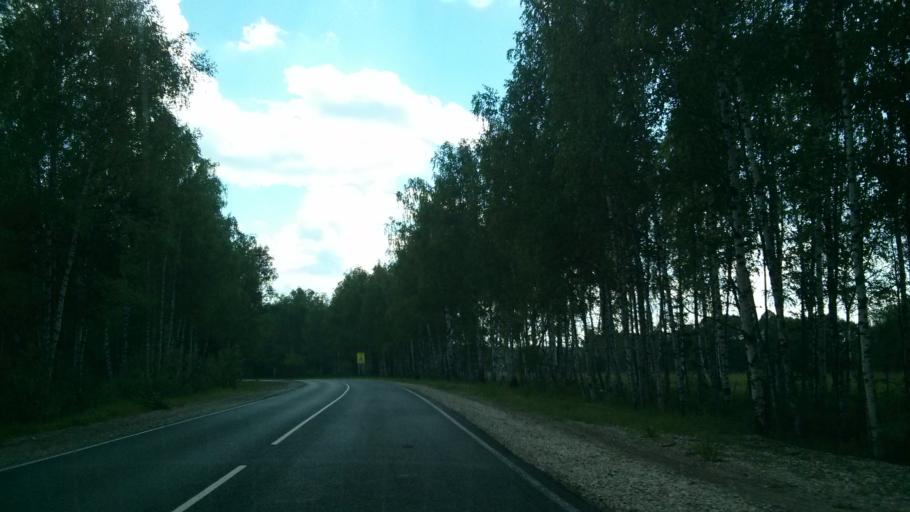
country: RU
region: Vladimir
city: Murom
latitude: 55.5154
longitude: 41.9287
